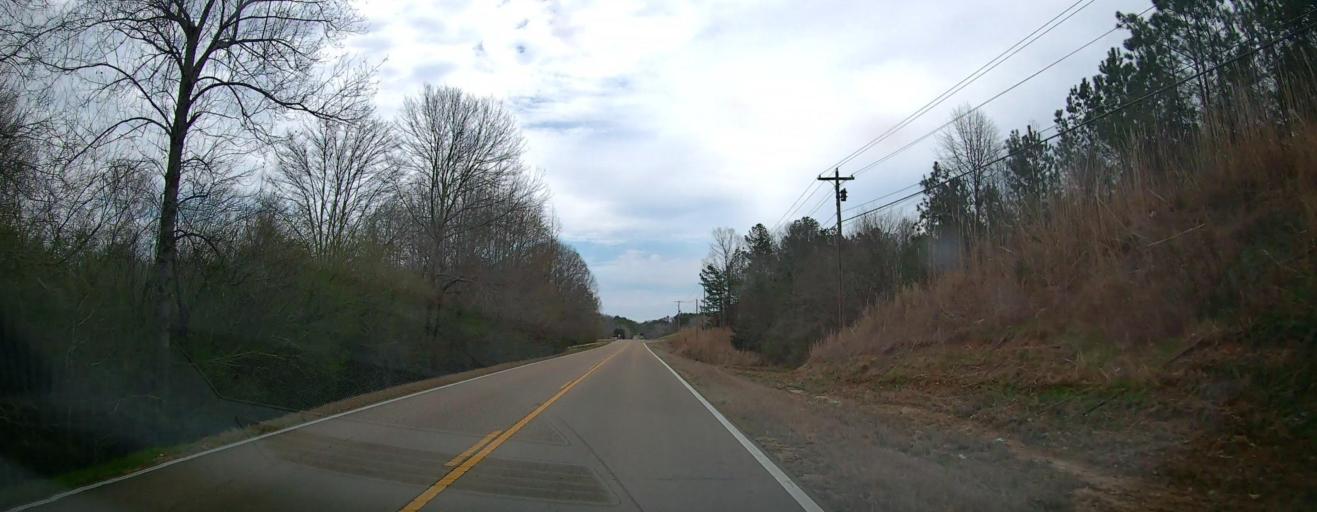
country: US
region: Mississippi
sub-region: Itawamba County
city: Fulton
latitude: 34.2554
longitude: -88.3121
